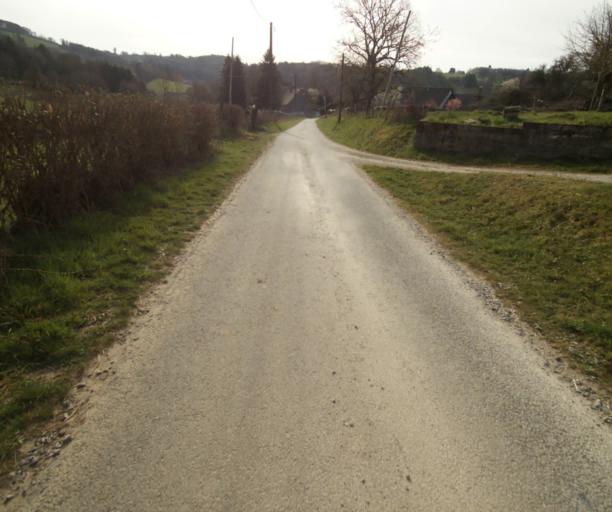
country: FR
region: Limousin
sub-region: Departement de la Correze
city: Chamboulive
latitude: 45.4467
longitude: 1.7516
